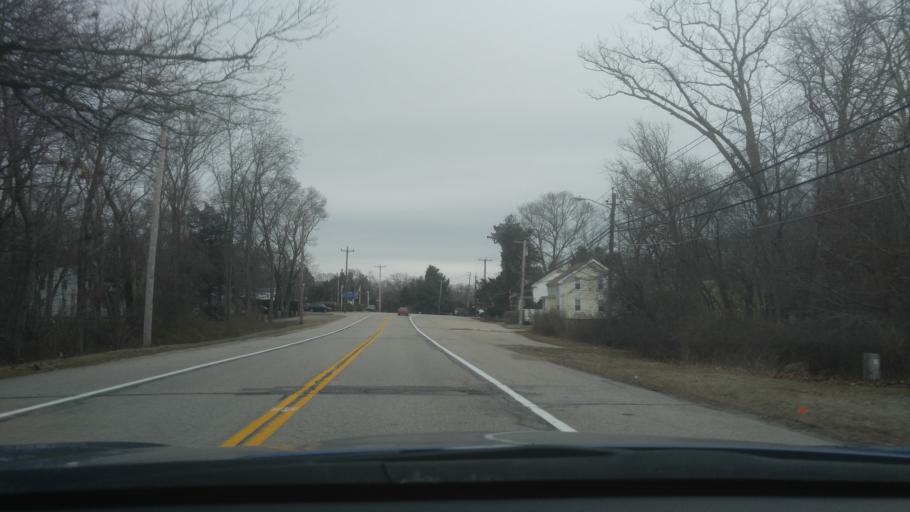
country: US
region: Rhode Island
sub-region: Washington County
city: North Kingstown
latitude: 41.5562
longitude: -71.4421
